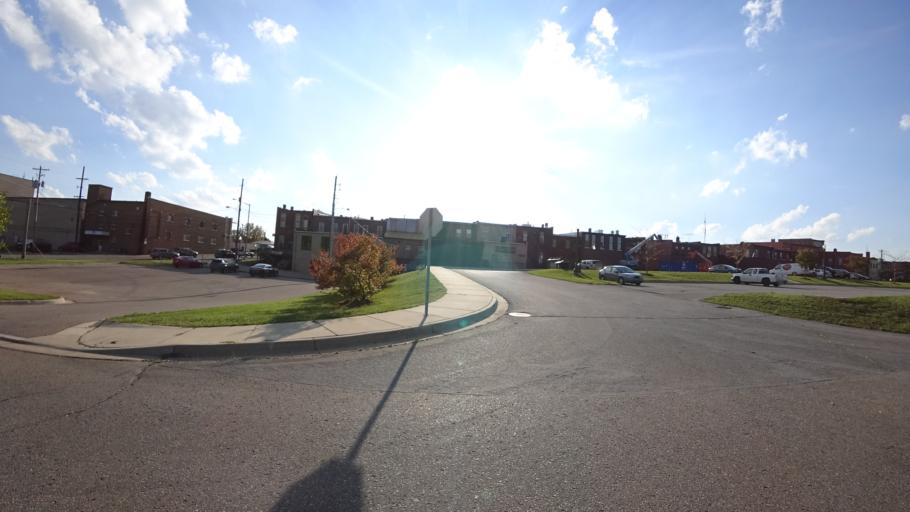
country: US
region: Michigan
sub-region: Saint Joseph County
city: Three Rivers
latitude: 41.9449
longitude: -85.6321
